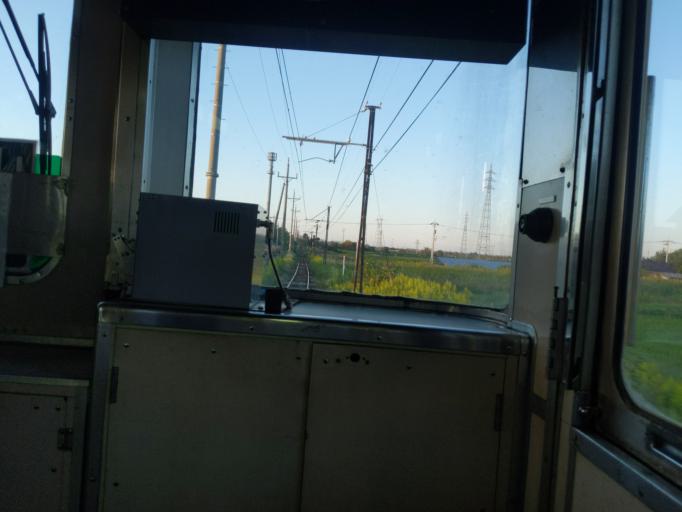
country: JP
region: Toyama
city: Kamiichi
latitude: 36.6926
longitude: 137.3182
